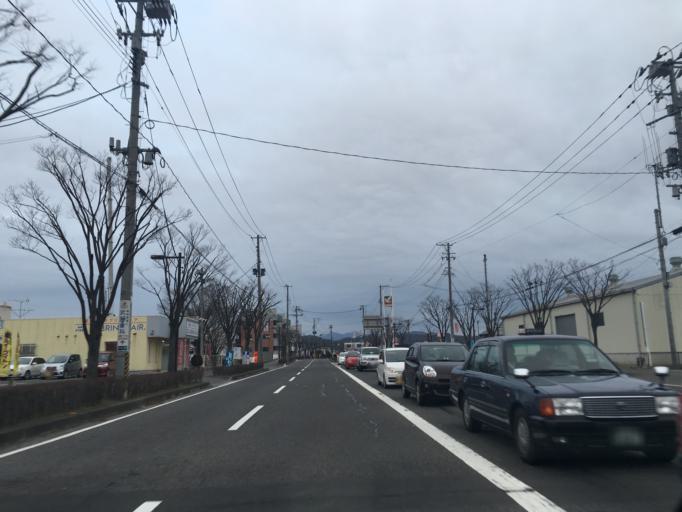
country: JP
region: Fukushima
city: Koriyama
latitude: 37.4004
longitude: 140.3966
